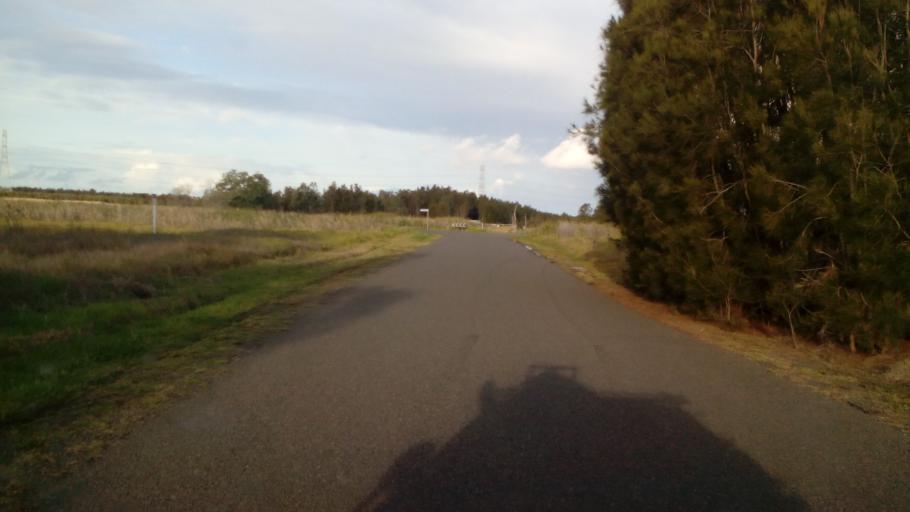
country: AU
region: New South Wales
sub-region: Newcastle
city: Mayfield West
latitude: -32.8452
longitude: 151.7013
